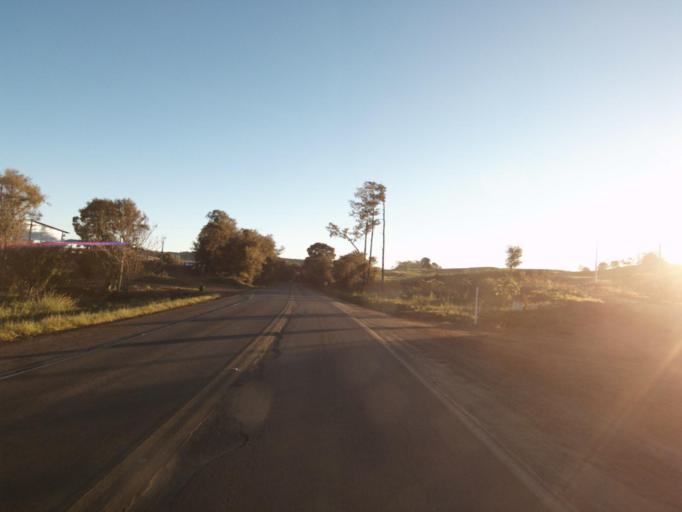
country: BR
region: Santa Catarina
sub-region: Sao Lourenco Do Oeste
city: Sao Lourenco dOeste
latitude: -26.8259
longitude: -53.0948
